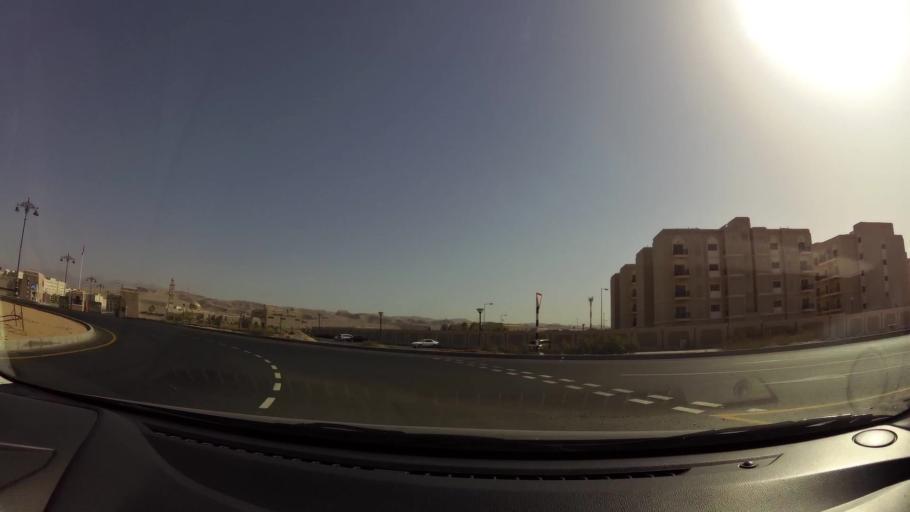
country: OM
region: Muhafazat Masqat
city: Bawshar
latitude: 23.5745
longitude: 58.2787
